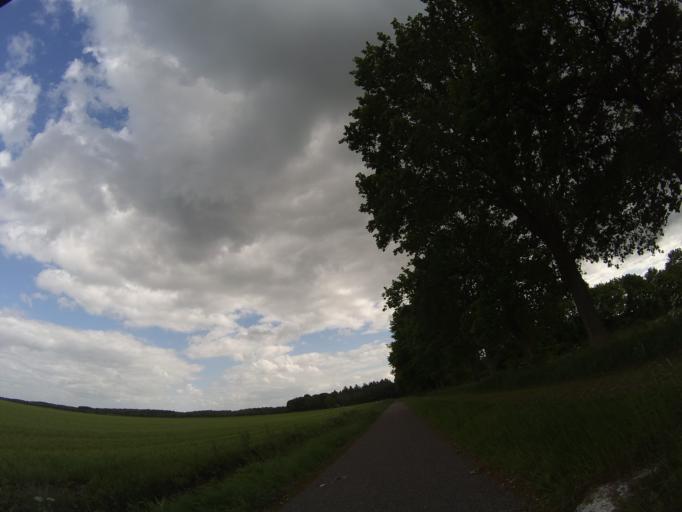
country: NL
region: Drenthe
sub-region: Gemeente Emmen
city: Emmen
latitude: 52.8580
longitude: 6.8702
